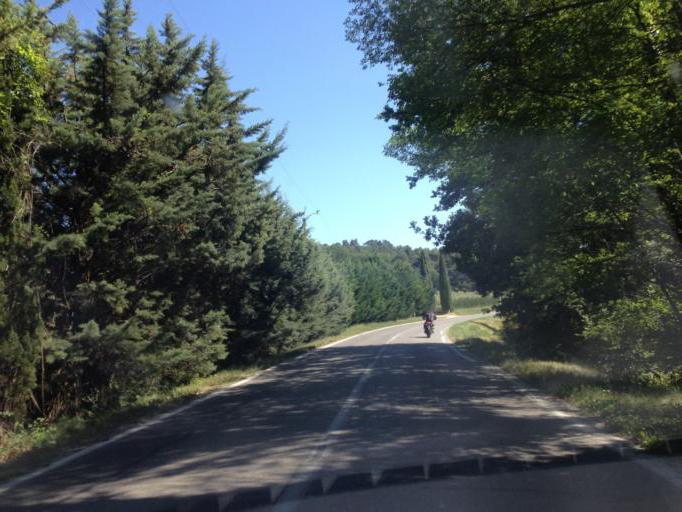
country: FR
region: Provence-Alpes-Cote d'Azur
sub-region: Departement du Vaucluse
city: Lourmarin
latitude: 43.7585
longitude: 5.3656
